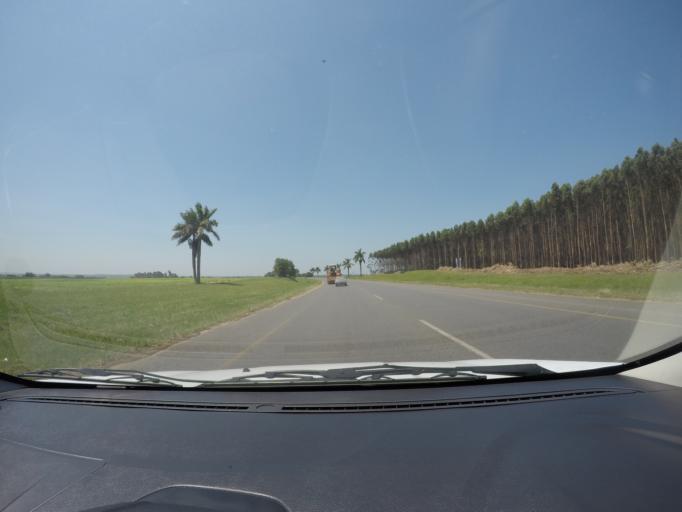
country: ZA
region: KwaZulu-Natal
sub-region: uThungulu District Municipality
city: eSikhawini
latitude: -28.8161
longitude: 31.9538
